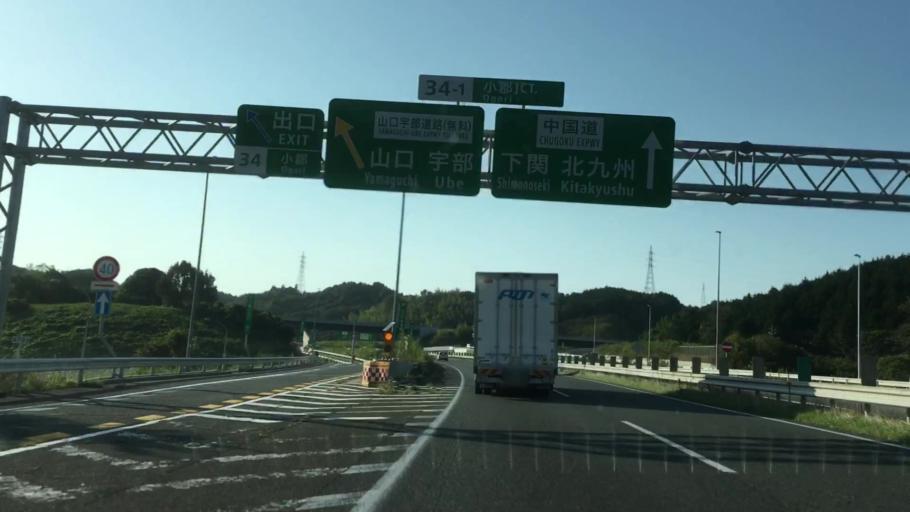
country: JP
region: Yamaguchi
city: Ogori-shimogo
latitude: 34.1254
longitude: 131.4065
